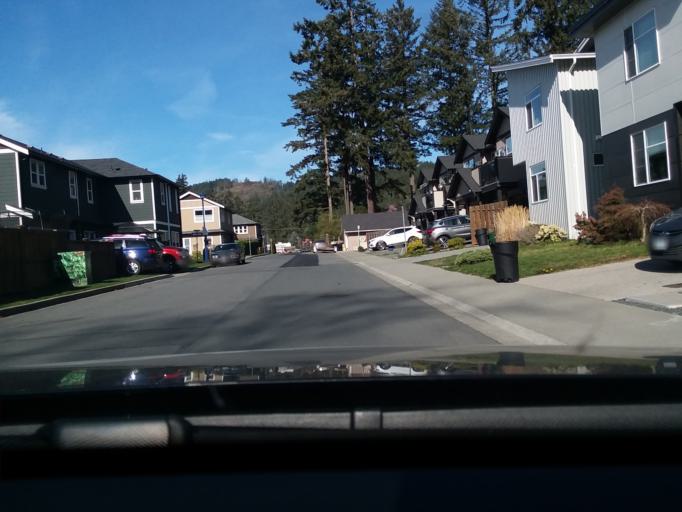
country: CA
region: British Columbia
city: Langford
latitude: 48.4283
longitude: -123.5319
